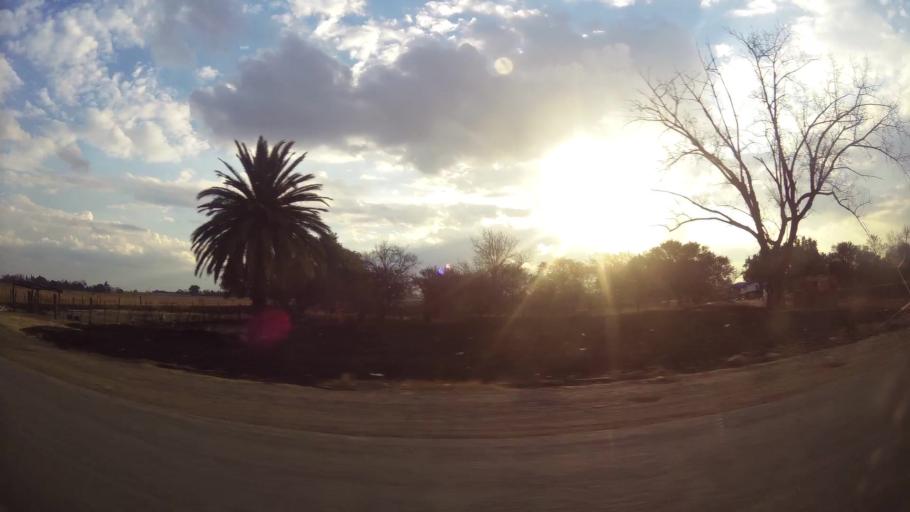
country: ZA
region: Gauteng
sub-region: Sedibeng District Municipality
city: Vanderbijlpark
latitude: -26.6318
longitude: 27.8086
